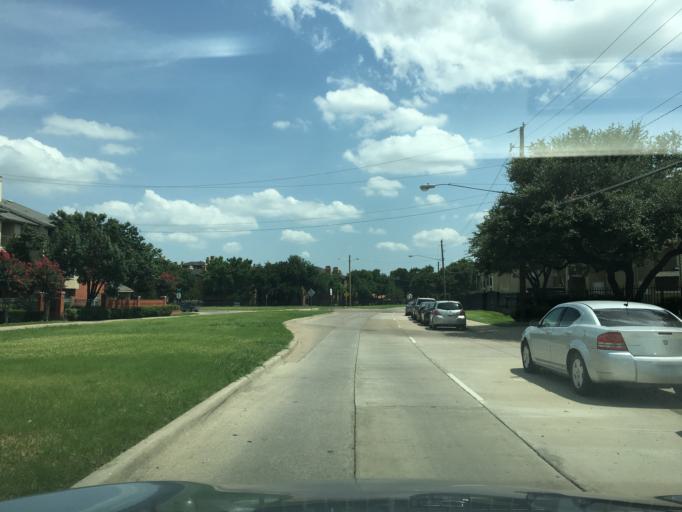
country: US
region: Texas
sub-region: Dallas County
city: Addison
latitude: 32.9442
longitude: -96.8184
